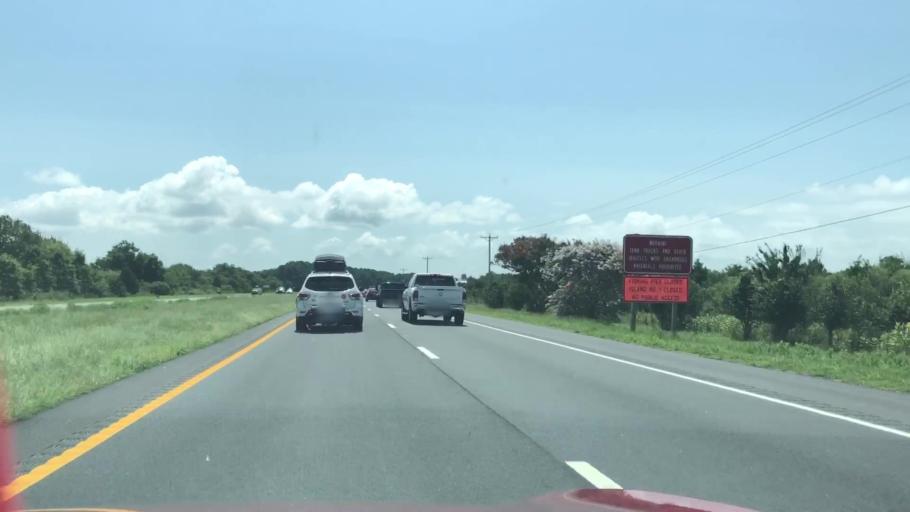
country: US
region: Virginia
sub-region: Northampton County
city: Cape Charles
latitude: 37.1429
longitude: -75.9698
